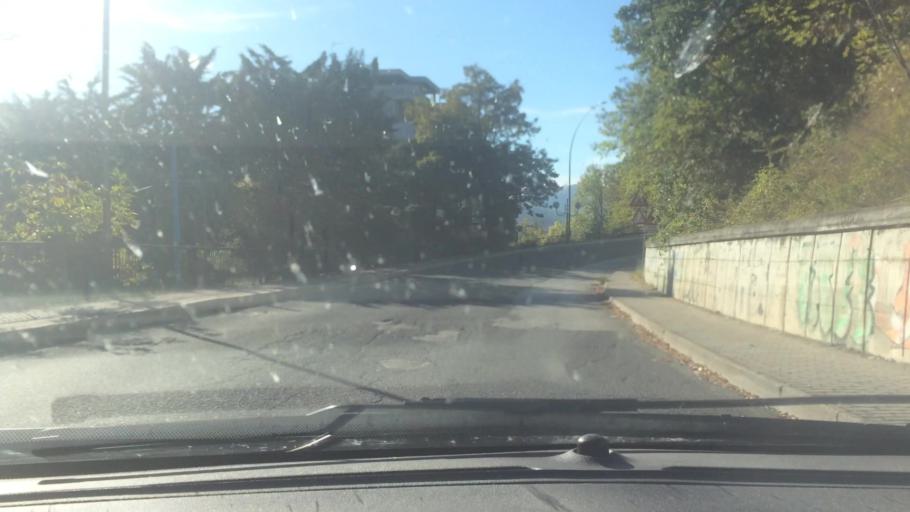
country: IT
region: Basilicate
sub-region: Provincia di Potenza
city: Potenza
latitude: 40.6426
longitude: 15.7965
